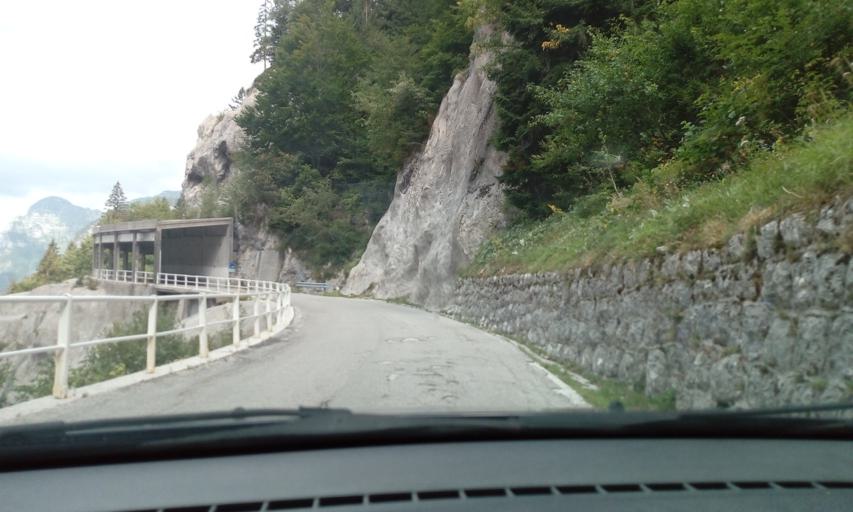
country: SI
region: Bovec
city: Bovec
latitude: 46.3902
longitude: 13.4689
